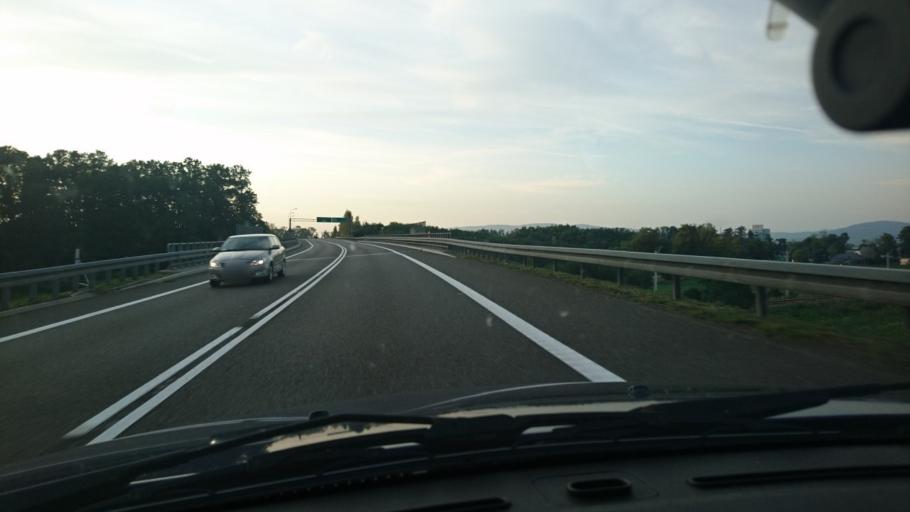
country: PL
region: Silesian Voivodeship
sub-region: Powiat zywiecki
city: Wieprz
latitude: 49.6546
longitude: 19.1699
